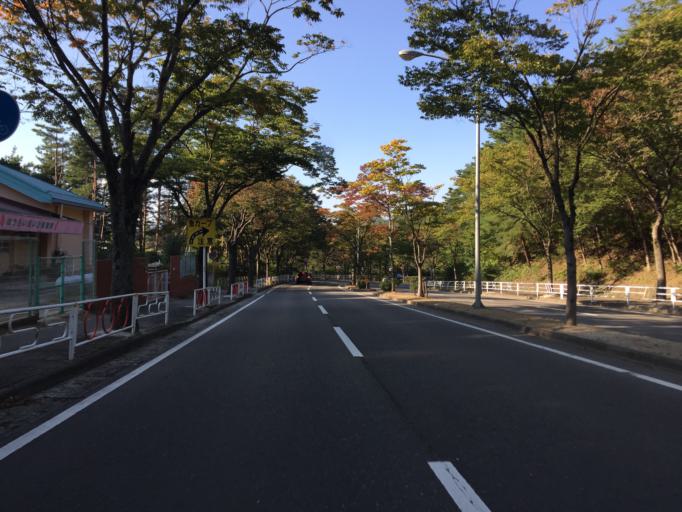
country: JP
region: Fukushima
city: Fukushima-shi
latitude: 37.7002
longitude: 140.4711
